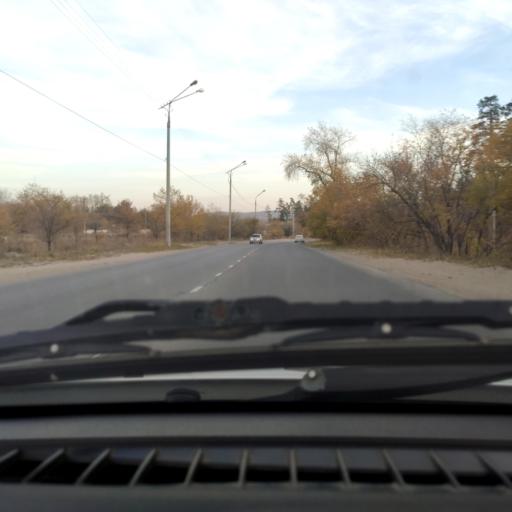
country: RU
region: Samara
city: Zhigulevsk
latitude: 53.4700
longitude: 49.5453
